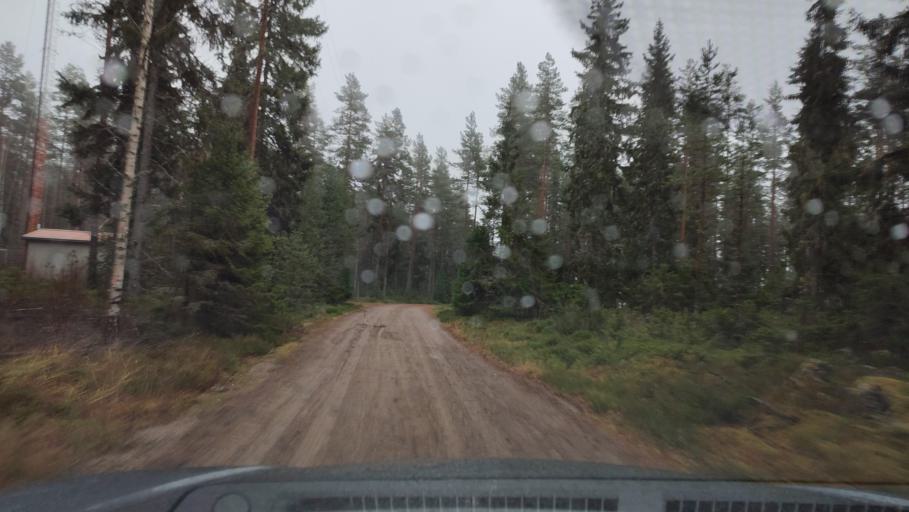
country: FI
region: Southern Ostrobothnia
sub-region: Suupohja
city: Karijoki
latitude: 62.1974
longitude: 21.7816
